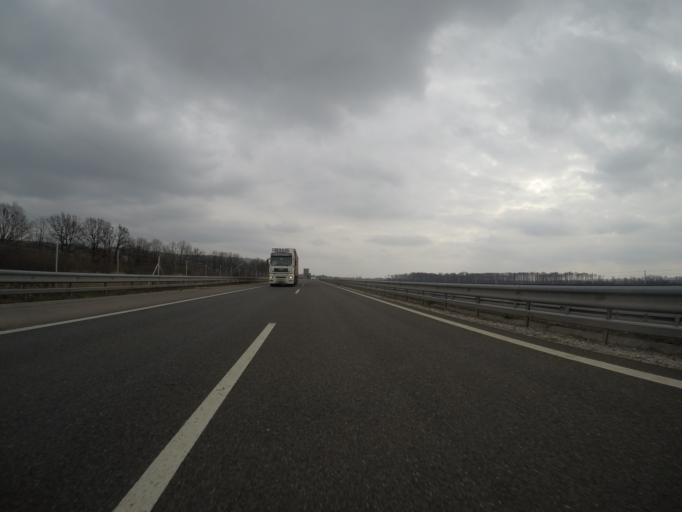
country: SI
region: Lendava-Lendva
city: Lendava
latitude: 46.5816
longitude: 16.4352
